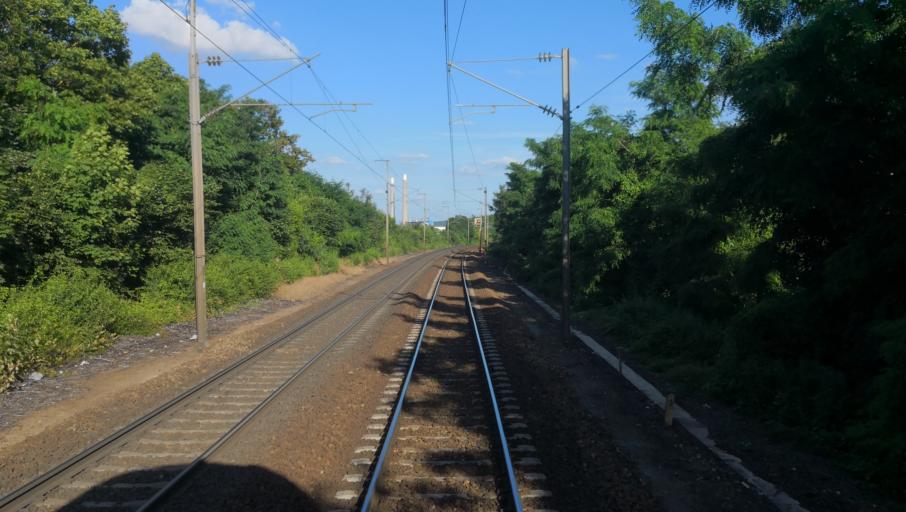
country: FR
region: Ile-de-France
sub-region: Departement des Yvelines
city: Mantes-la-Jolie
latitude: 48.9797
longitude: 1.7254
